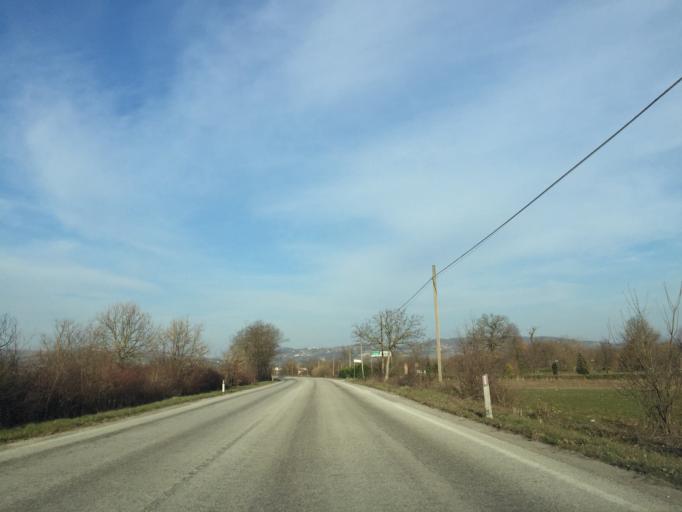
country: IT
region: Molise
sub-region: Provincia di Campobasso
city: San Massimo
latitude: 41.5052
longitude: 14.4268
